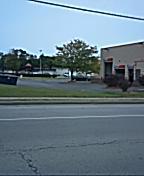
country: US
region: Kentucky
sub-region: Jefferson County
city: Middletown
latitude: 38.2453
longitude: -85.5244
